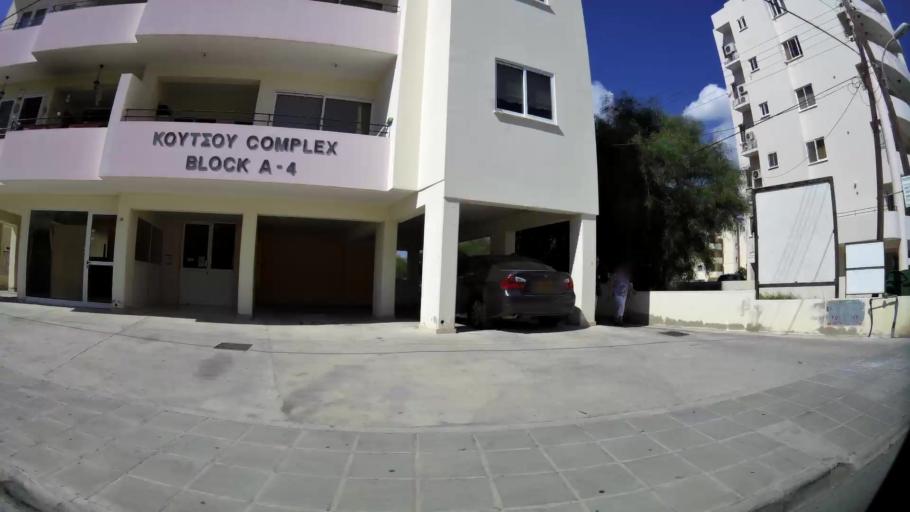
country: CY
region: Larnaka
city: Larnaca
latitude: 34.9030
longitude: 33.6349
